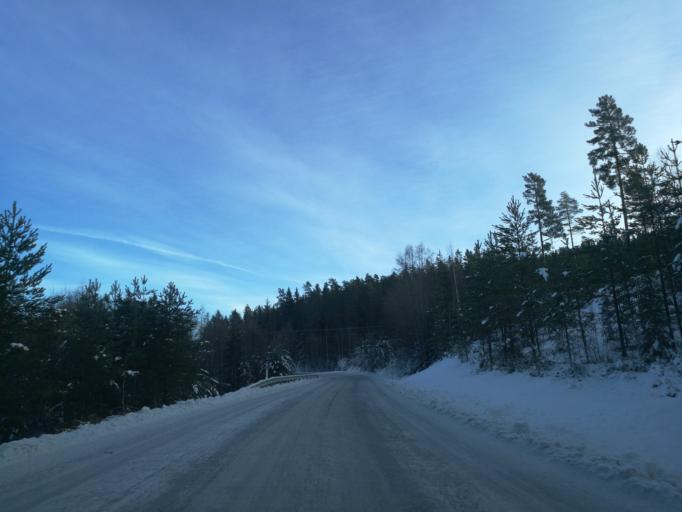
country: NO
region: Hedmark
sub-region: Grue
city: Kirkenaer
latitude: 60.3428
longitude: 12.2994
